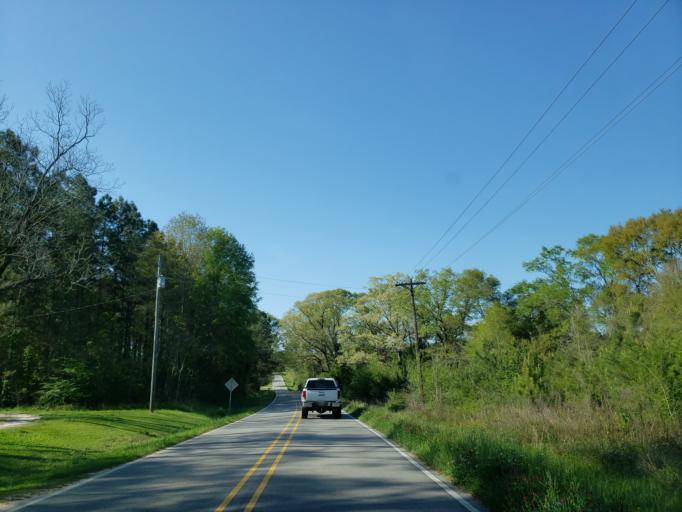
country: US
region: Mississippi
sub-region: Covington County
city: Collins
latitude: 31.6144
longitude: -89.3882
